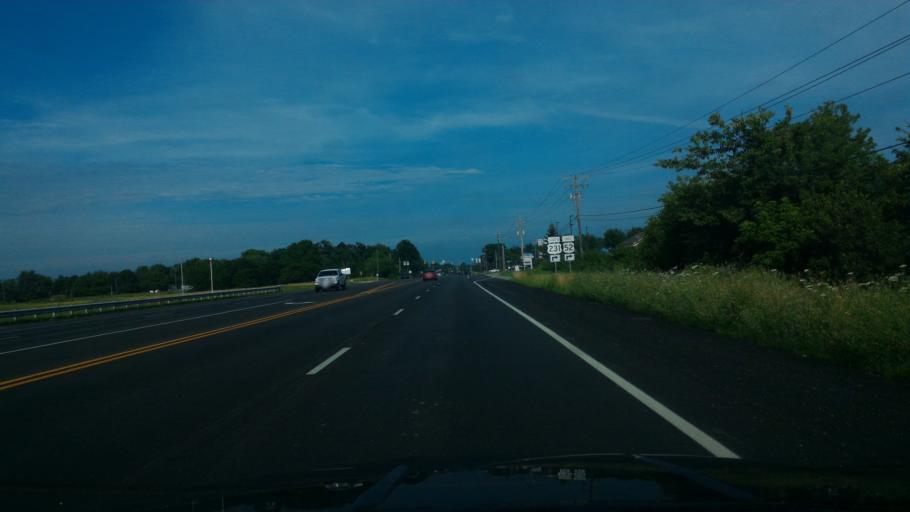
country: US
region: Indiana
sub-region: Tippecanoe County
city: West Lafayette
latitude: 40.4674
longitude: -86.9576
